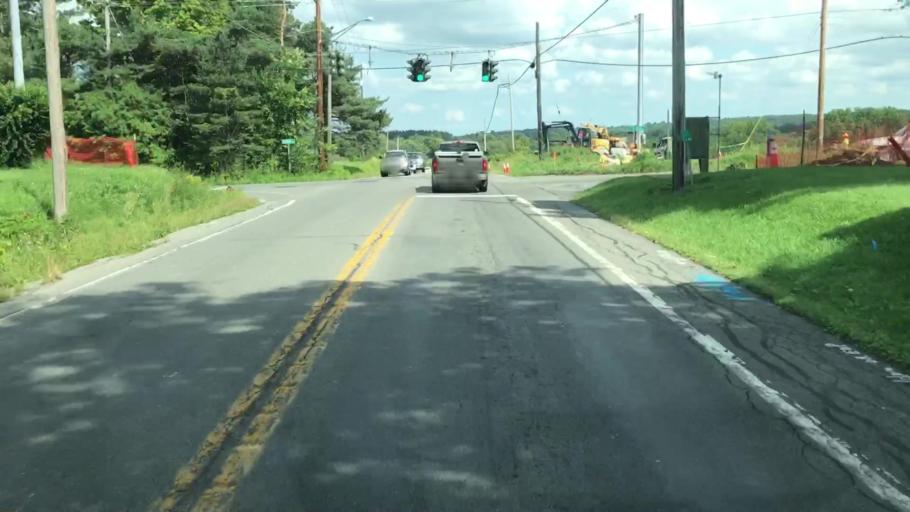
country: US
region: New York
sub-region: Onondaga County
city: Fairmount
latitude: 42.9867
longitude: -76.2606
